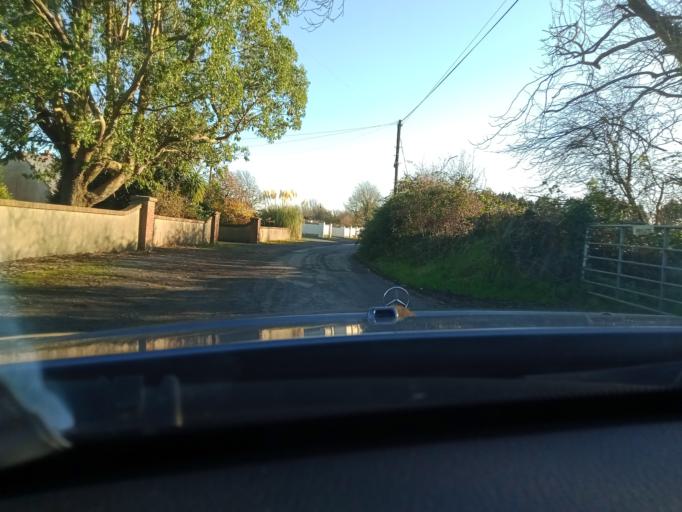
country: IE
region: Leinster
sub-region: Kilkenny
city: Mooncoin
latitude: 52.2945
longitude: -7.1832
